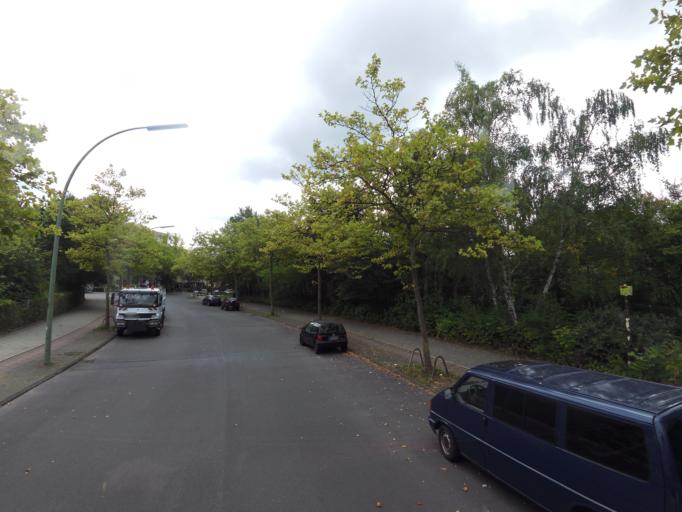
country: DE
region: Berlin
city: Lichterfelde
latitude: 52.4115
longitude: 13.3039
